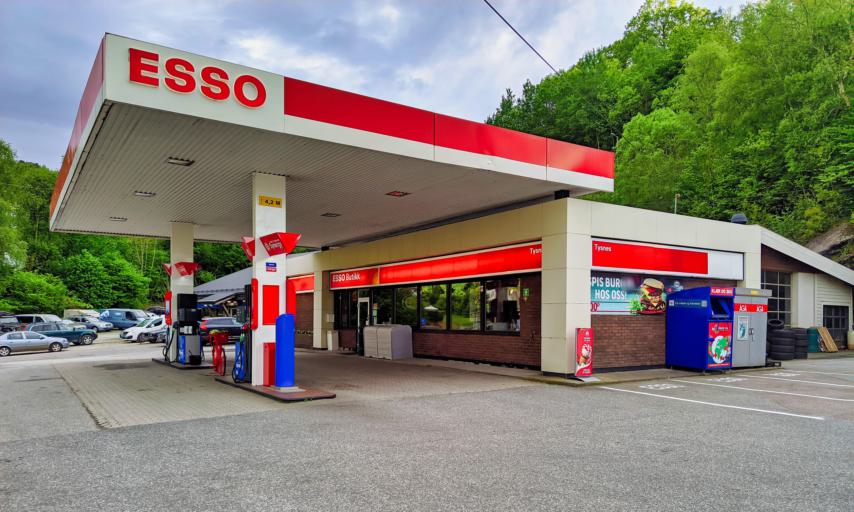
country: NO
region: Hordaland
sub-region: Tysnes
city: Uggdal
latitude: 60.0424
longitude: 5.5228
